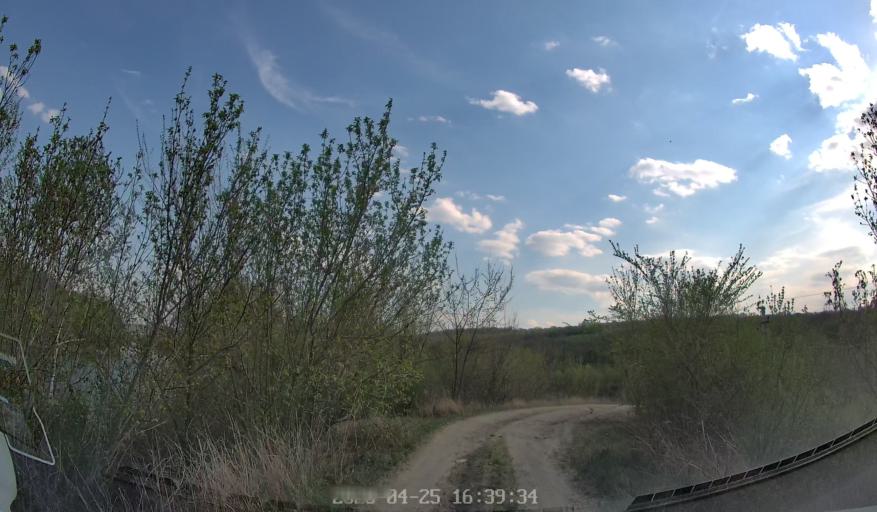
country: MD
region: Chisinau
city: Vadul lui Voda
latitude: 47.1087
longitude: 29.0641
